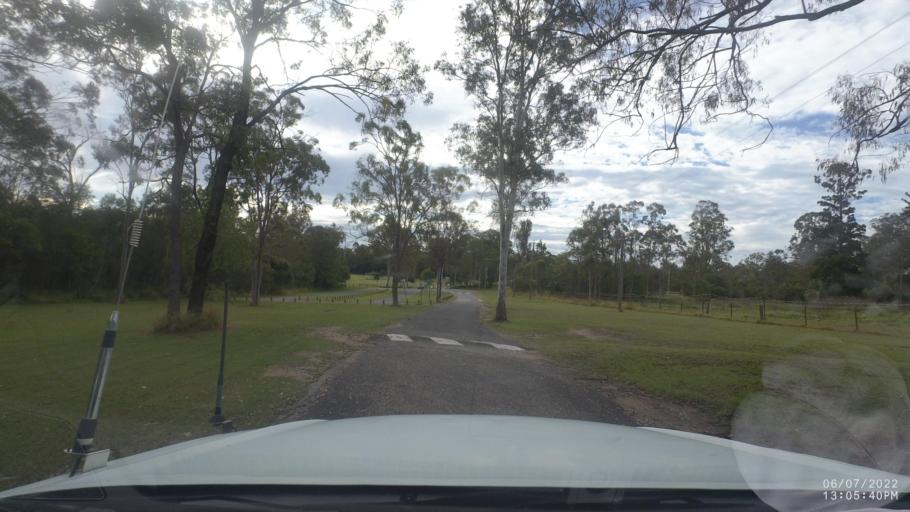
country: AU
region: Queensland
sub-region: Logan
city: Cedar Vale
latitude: -27.8476
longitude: 153.0294
